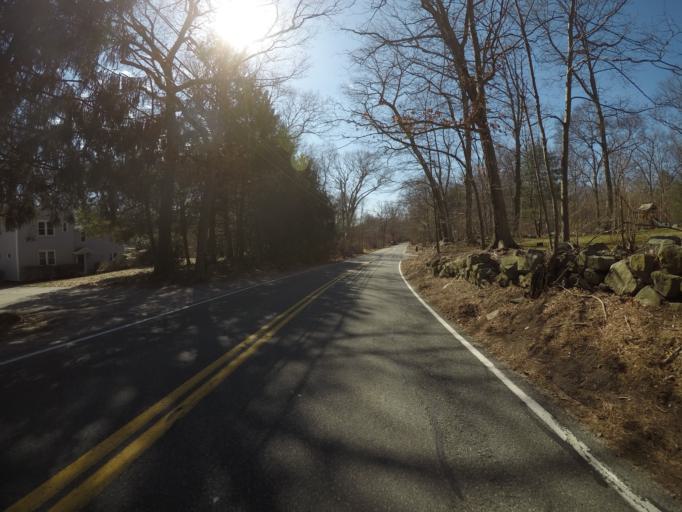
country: US
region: Massachusetts
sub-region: Norfolk County
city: Stoughton
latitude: 42.0870
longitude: -71.1383
